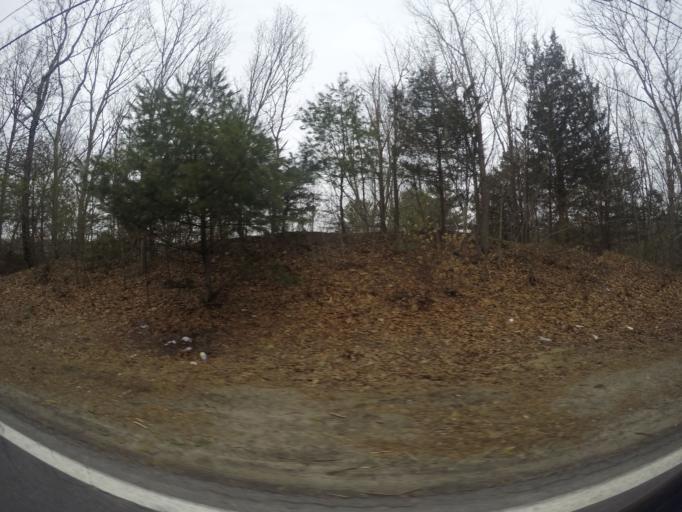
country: US
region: Massachusetts
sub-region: Bristol County
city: Easton
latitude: 42.0093
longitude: -71.0759
